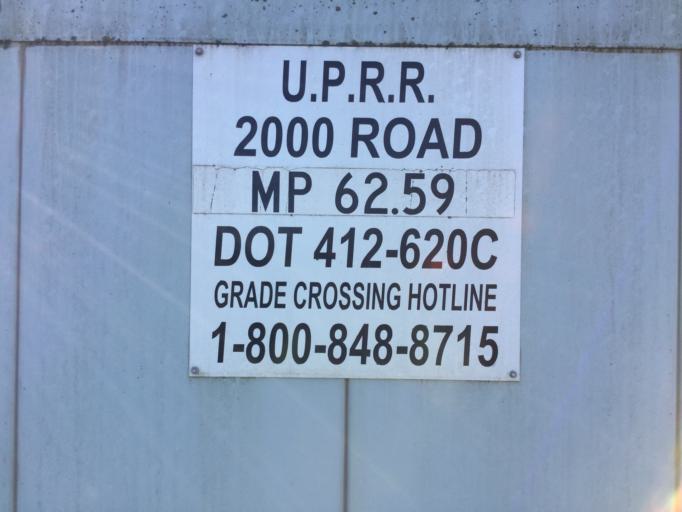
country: US
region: Kansas
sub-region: Miami County
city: Osawatomie
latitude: 38.3166
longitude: -94.9980
